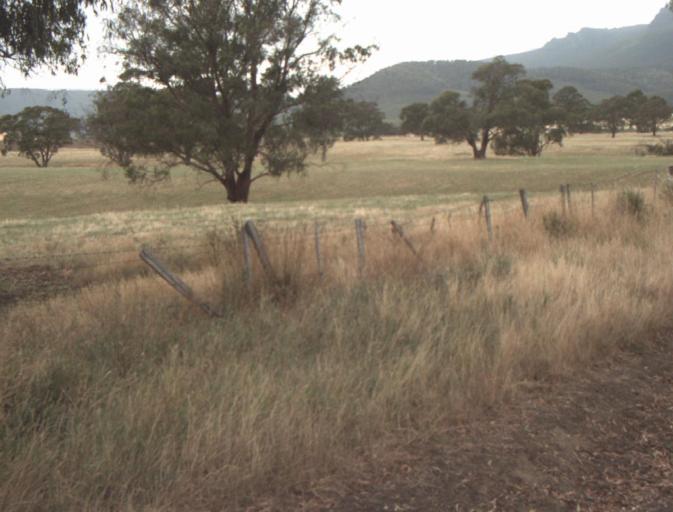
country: AU
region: Tasmania
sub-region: Dorset
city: Scottsdale
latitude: -41.4650
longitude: 147.5726
